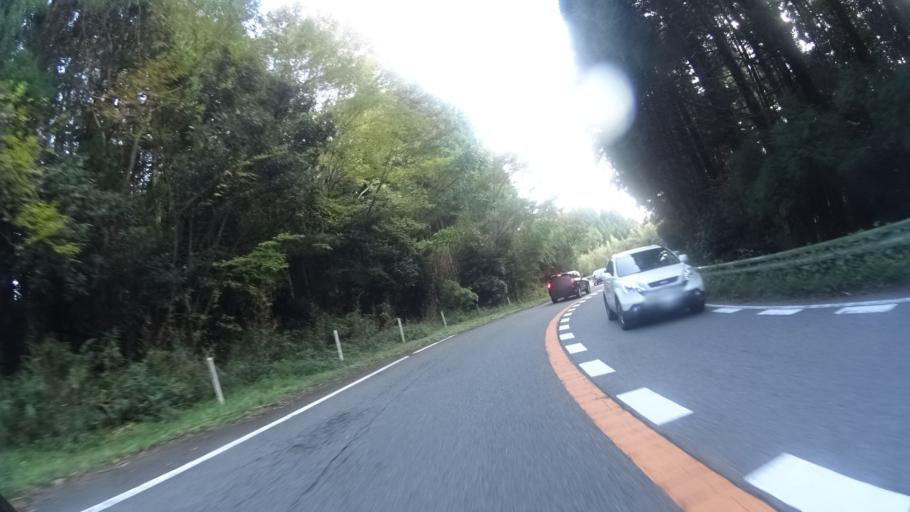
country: JP
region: Oita
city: Beppu
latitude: 33.2699
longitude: 131.4303
